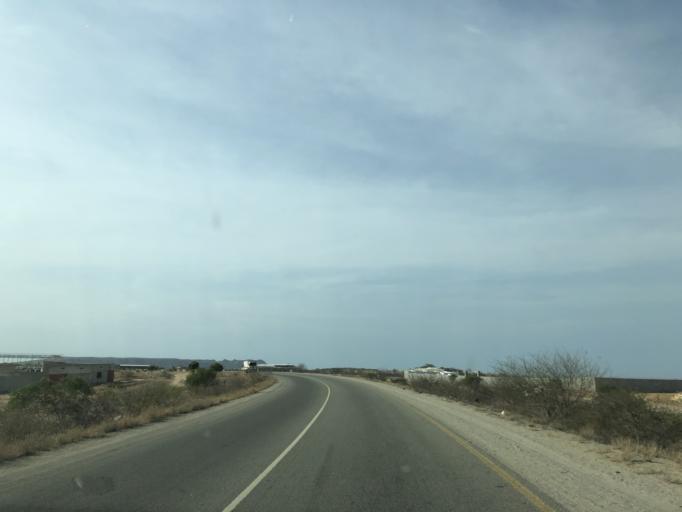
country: AO
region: Benguela
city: Benguela
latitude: -12.6945
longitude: 13.3454
